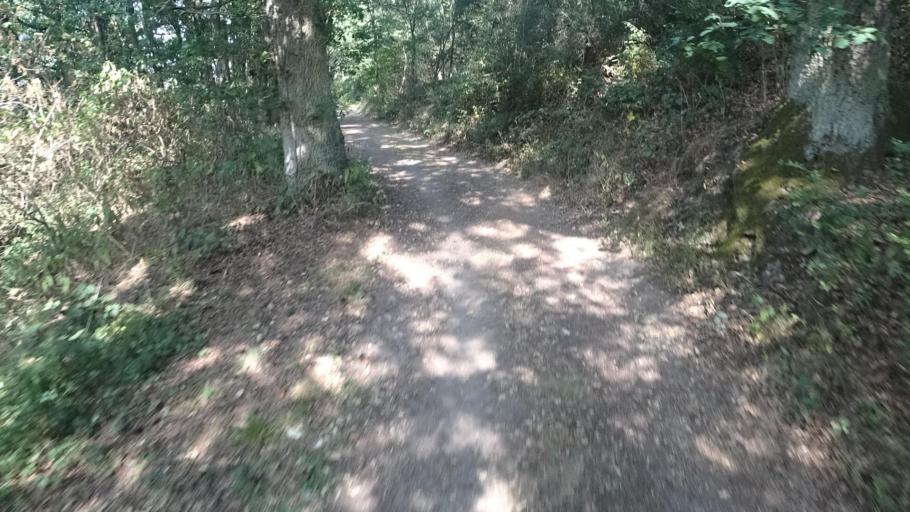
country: DE
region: Rheinland-Pfalz
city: Mutterschied
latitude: 49.9880
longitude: 7.5600
